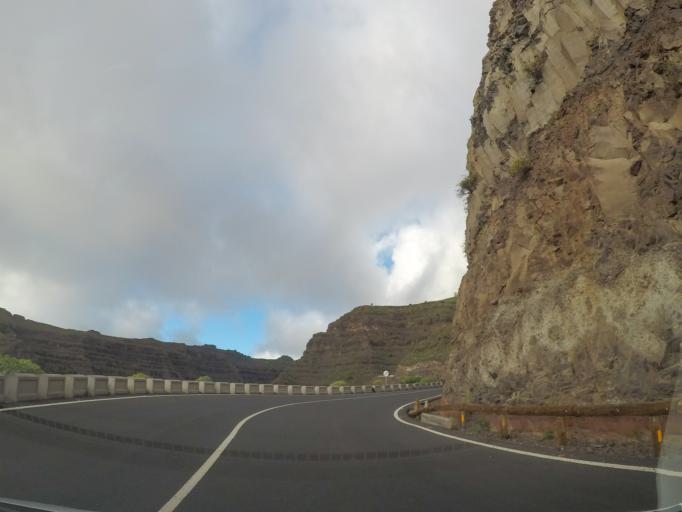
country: ES
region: Canary Islands
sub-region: Provincia de Santa Cruz de Tenerife
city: Vallehermosa
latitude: 28.1152
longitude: -17.3207
